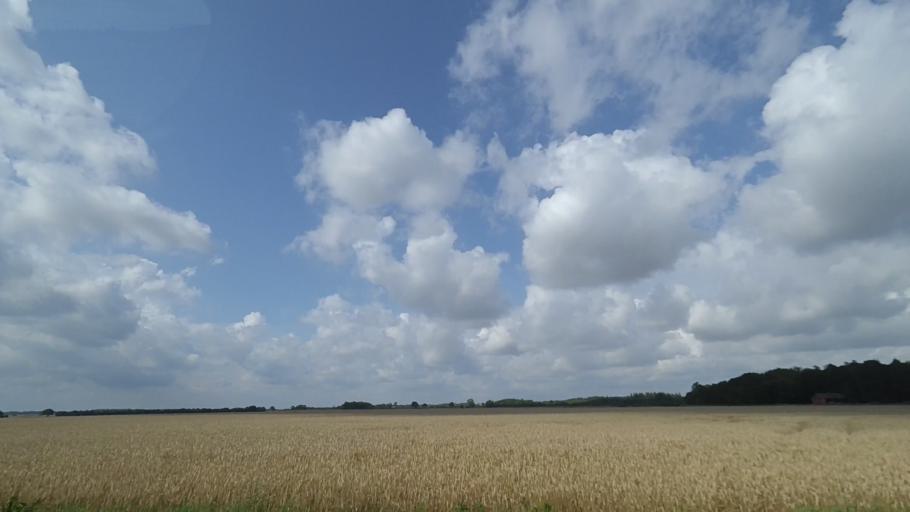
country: DK
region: Central Jutland
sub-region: Norddjurs Kommune
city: Auning
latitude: 56.5091
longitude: 10.4204
